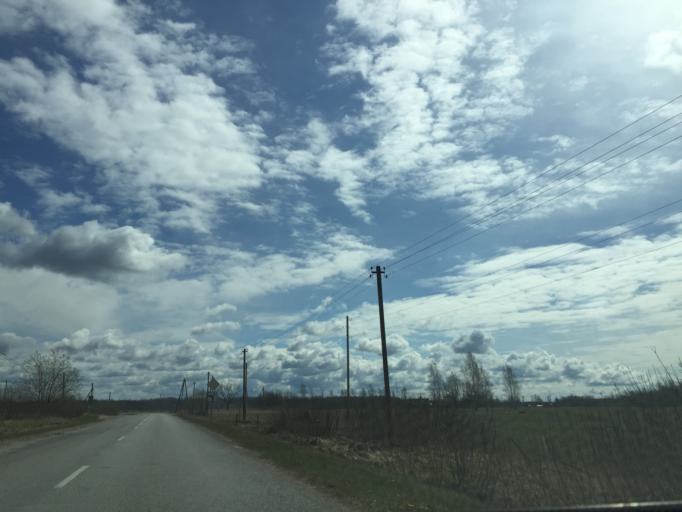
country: LV
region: Salacgrivas
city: Salacgriva
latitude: 57.7448
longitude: 24.3926
